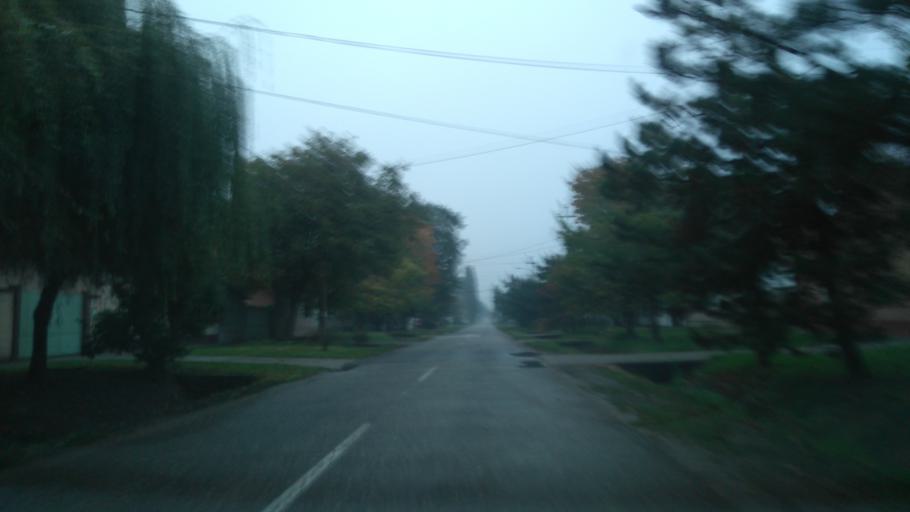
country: RS
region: Autonomna Pokrajina Vojvodina
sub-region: Juznobacki Okrug
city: Becej
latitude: 45.6153
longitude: 20.0388
